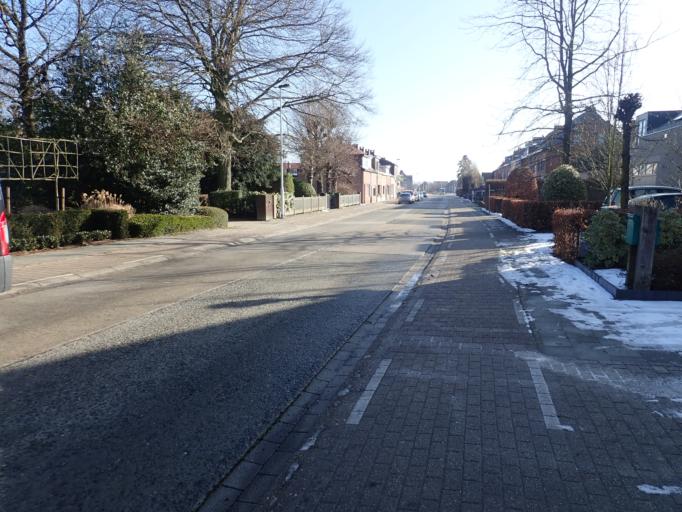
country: BE
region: Flanders
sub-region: Provincie Antwerpen
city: Boechout
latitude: 51.1669
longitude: 4.4993
